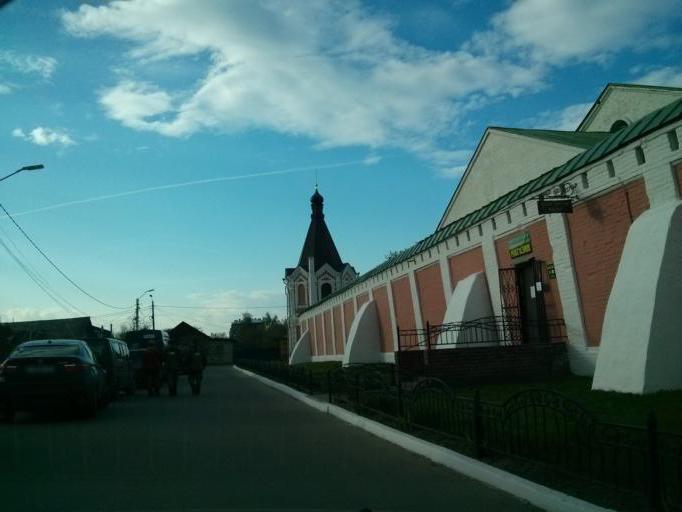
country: RU
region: Vladimir
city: Murom
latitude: 55.5725
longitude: 42.0646
